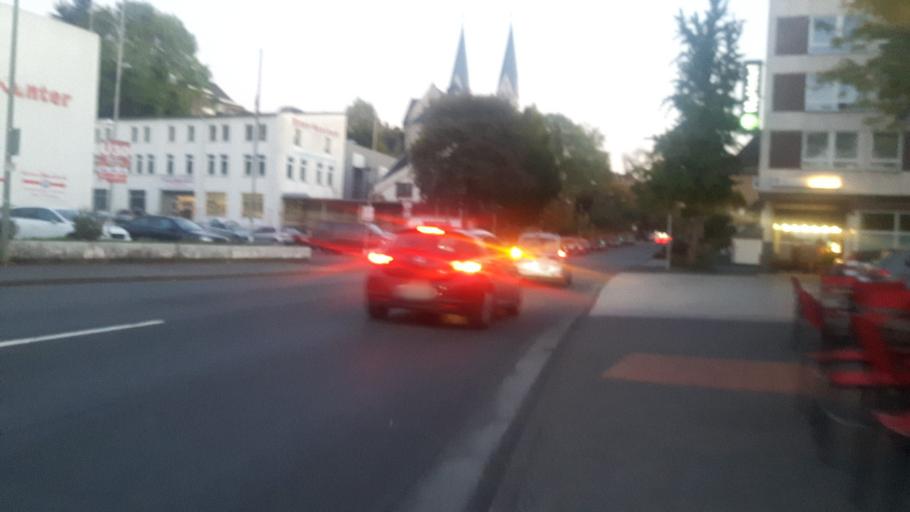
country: DE
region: North Rhine-Westphalia
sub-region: Regierungsbezirk Arnsberg
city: Siegen
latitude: 50.8816
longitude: 8.0296
